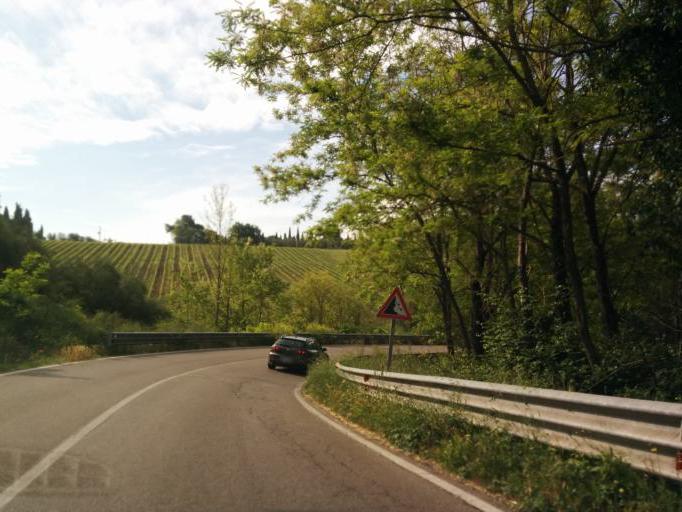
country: IT
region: Tuscany
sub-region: Province of Florence
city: San Casciano in Val di Pesa
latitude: 43.6511
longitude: 11.1914
